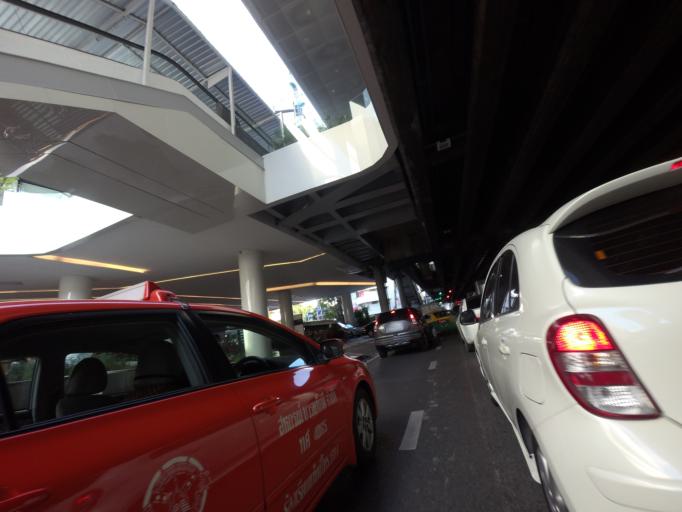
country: TH
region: Bangkok
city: Khlong Toei
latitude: 13.7310
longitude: 100.5693
